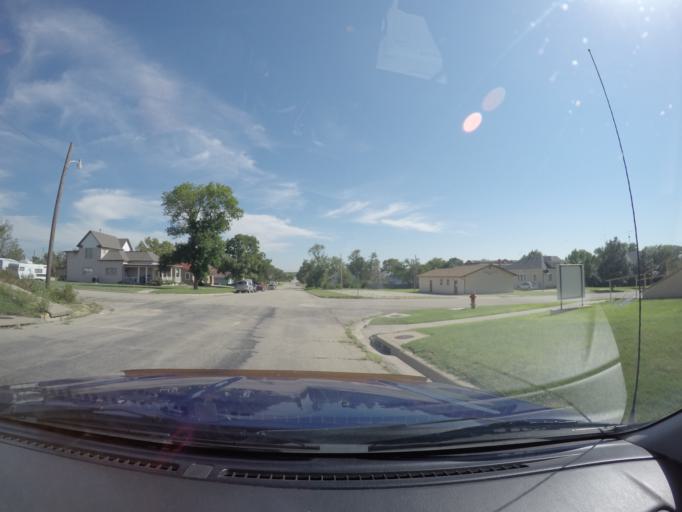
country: US
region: Kansas
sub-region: Rooks County
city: Stockton
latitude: 39.4391
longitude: -99.2709
